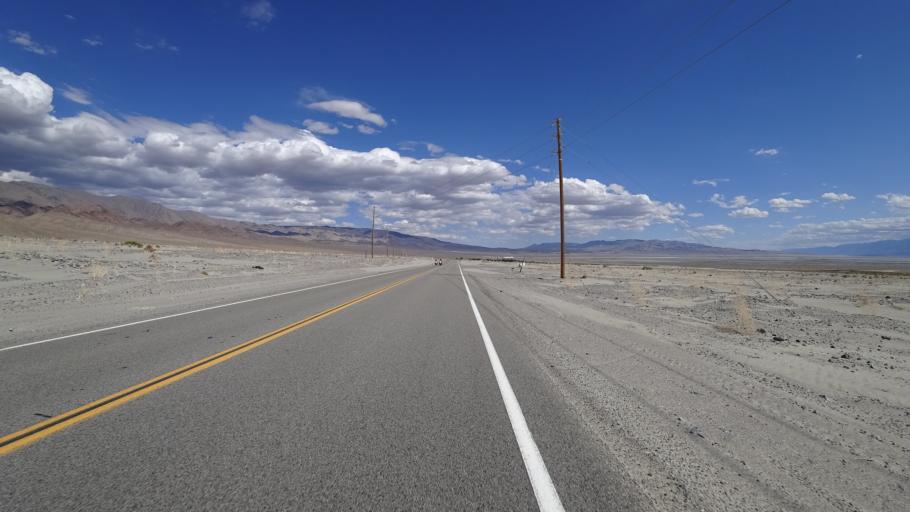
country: US
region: California
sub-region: Inyo County
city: Lone Pine
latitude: 36.5066
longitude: -117.8894
